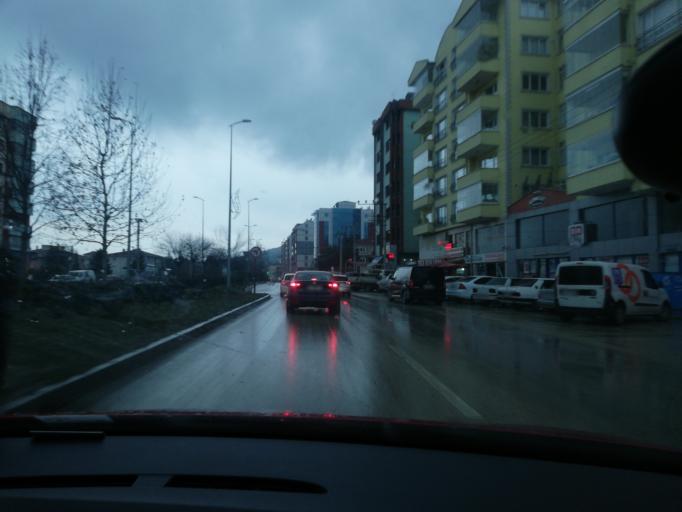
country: TR
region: Kastamonu
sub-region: Cide
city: Kastamonu
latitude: 41.4066
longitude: 33.7860
